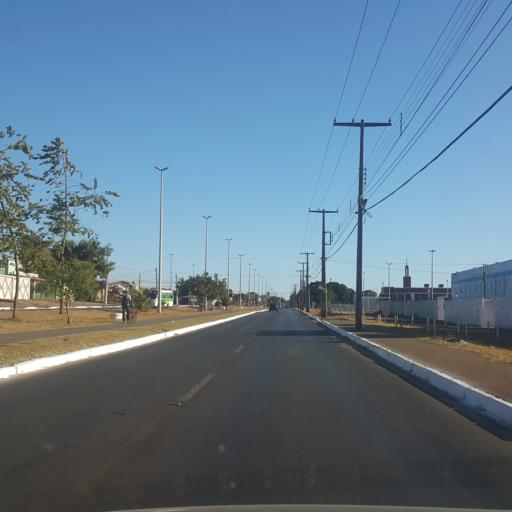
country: BR
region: Federal District
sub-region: Brasilia
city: Brasilia
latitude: -15.8296
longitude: -48.0915
